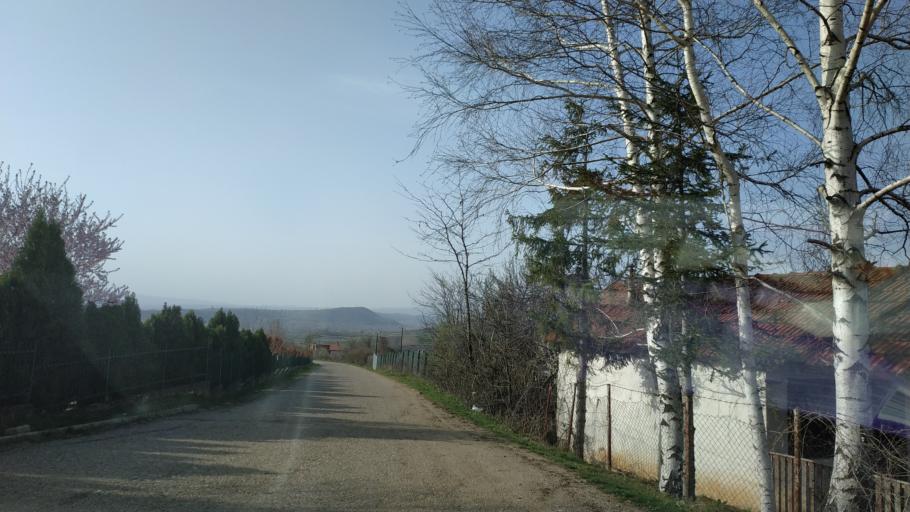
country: RS
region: Central Serbia
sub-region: Nisavski Okrug
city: Aleksinac
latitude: 43.5460
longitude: 21.7265
